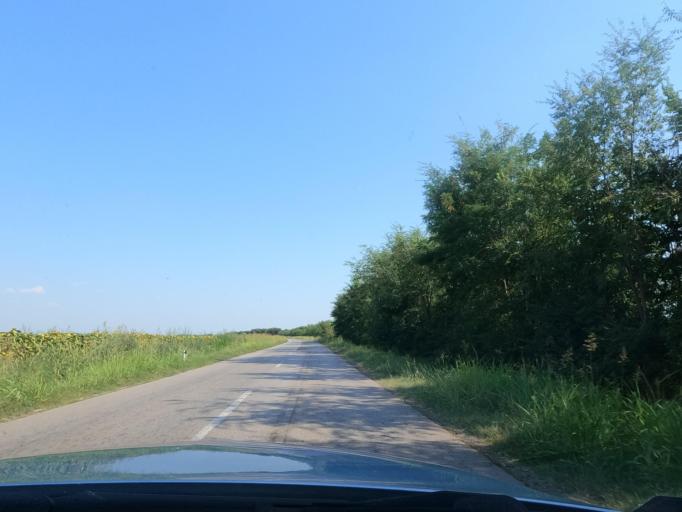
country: RS
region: Autonomna Pokrajina Vojvodina
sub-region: Juznobacki Okrug
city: Becej
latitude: 45.6566
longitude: 19.9611
